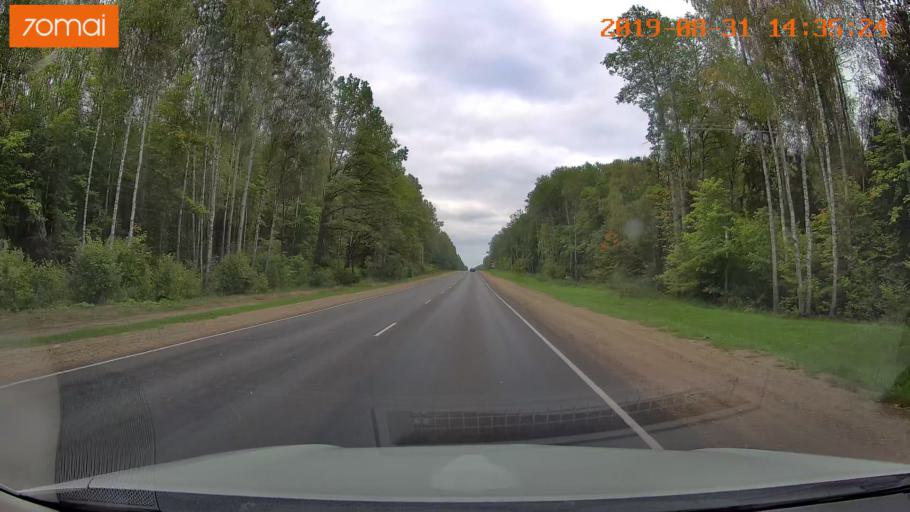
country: RU
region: Smolensk
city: Yekimovichi
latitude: 54.1626
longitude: 33.4549
